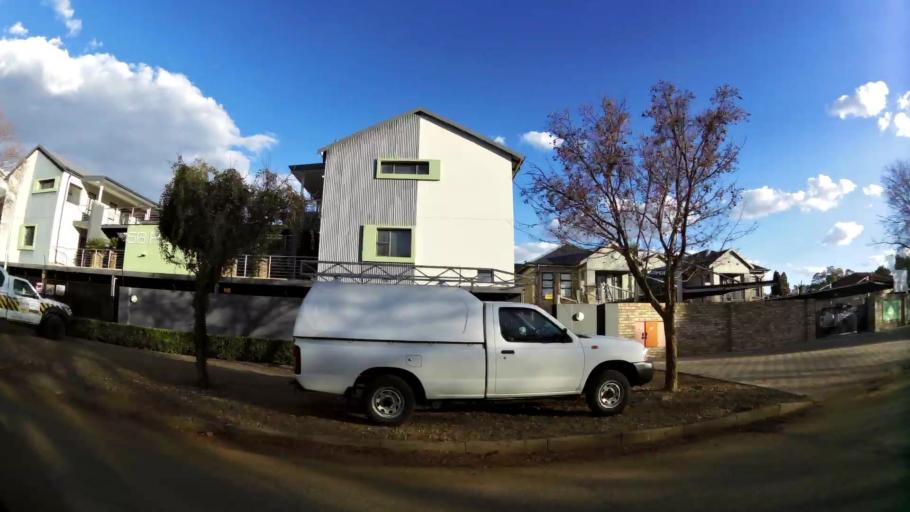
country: ZA
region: North-West
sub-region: Dr Kenneth Kaunda District Municipality
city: Potchefstroom
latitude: -26.6979
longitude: 27.0918
